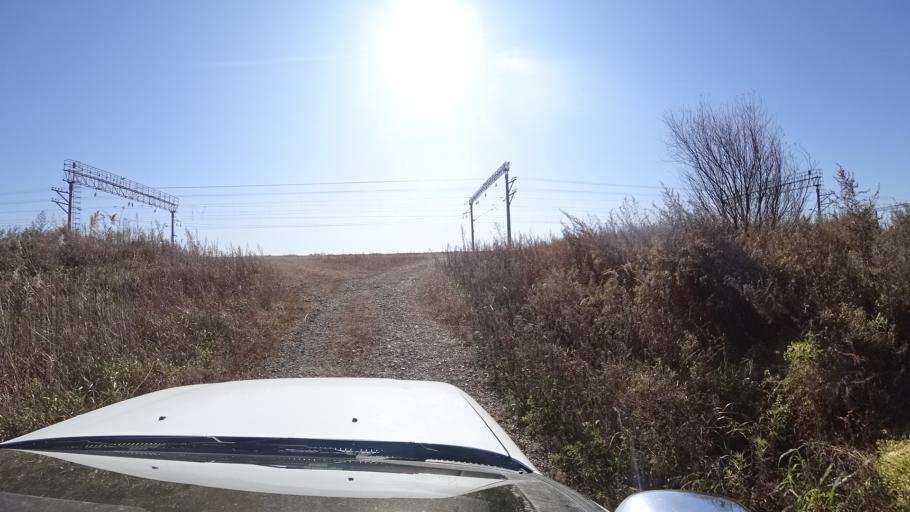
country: RU
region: Primorskiy
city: Dal'nerechensk
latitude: 45.9105
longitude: 133.7904
